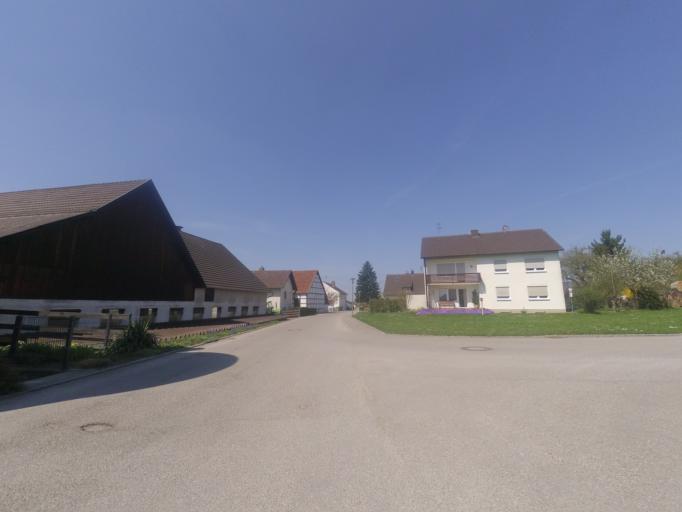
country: DE
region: Bavaria
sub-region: Swabia
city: Weissenhorn
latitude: 48.2786
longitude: 10.1650
